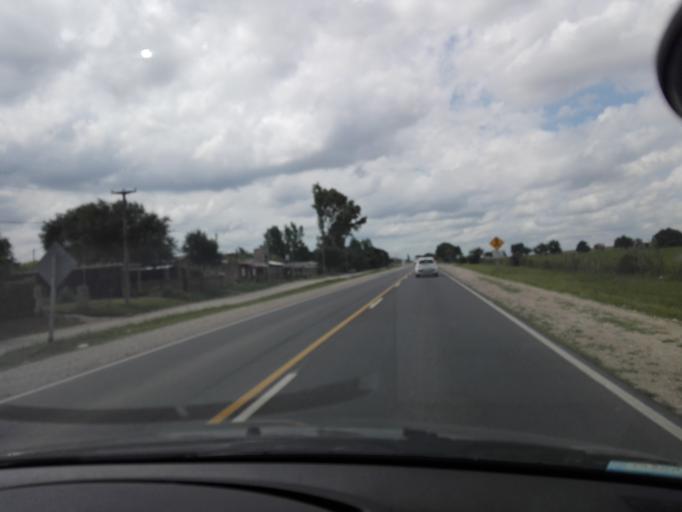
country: AR
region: Cordoba
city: Alta Gracia
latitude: -31.6315
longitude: -64.4356
